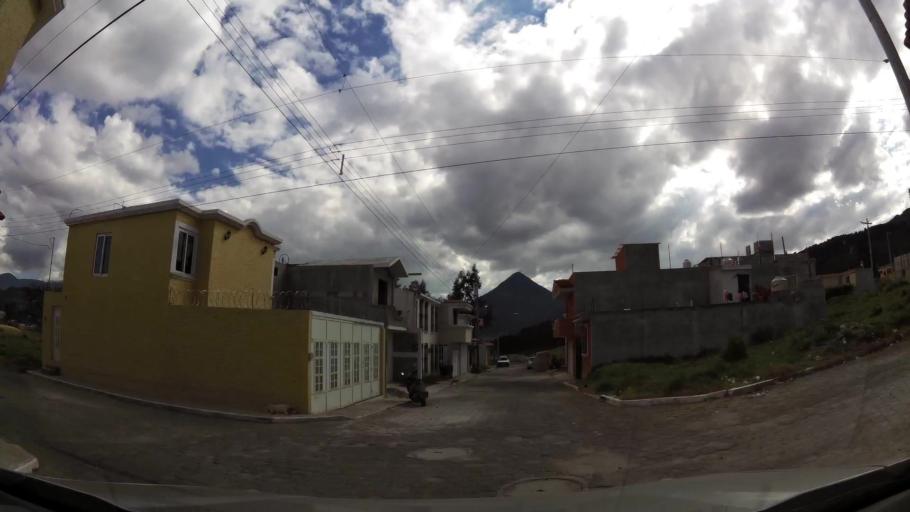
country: GT
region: Quetzaltenango
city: Quetzaltenango
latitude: 14.8348
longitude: -91.5490
